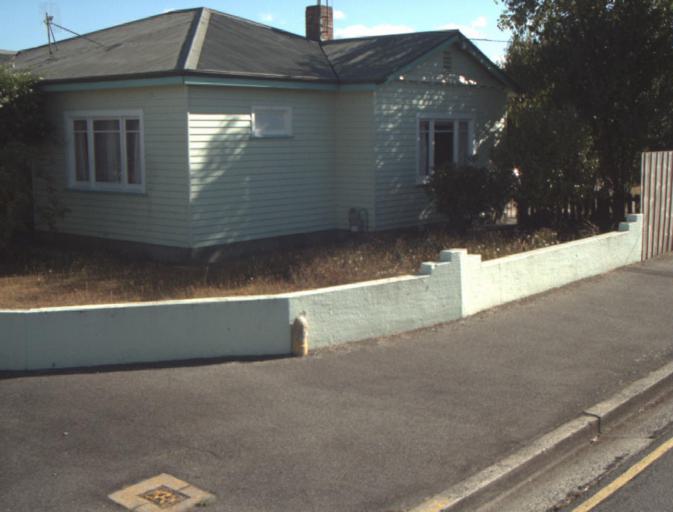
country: AU
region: Tasmania
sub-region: Launceston
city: Newnham
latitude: -41.4029
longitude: 147.1297
